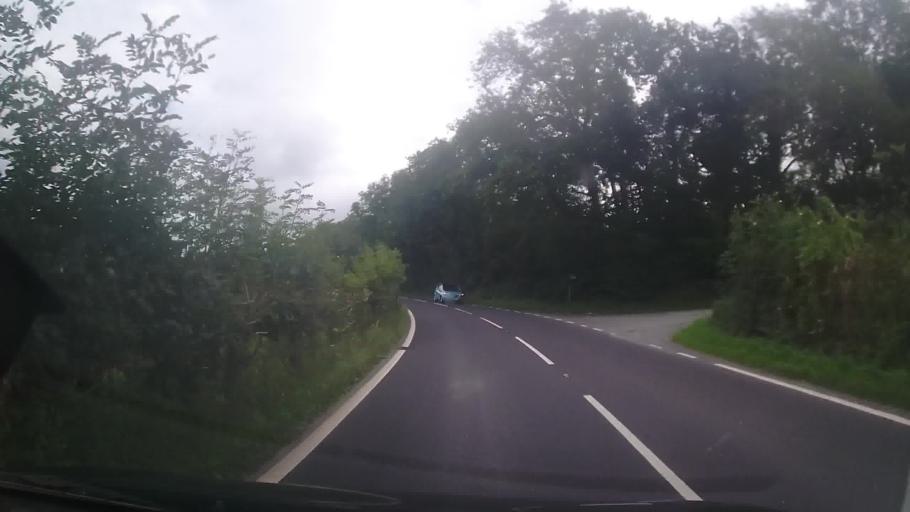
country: GB
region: Wales
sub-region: County of Ceredigion
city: Bow Street
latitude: 52.5284
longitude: -3.9599
